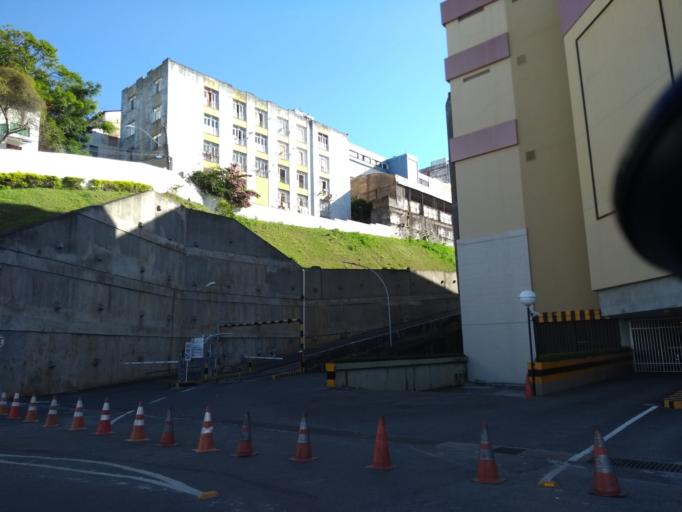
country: BR
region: Bahia
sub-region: Salvador
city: Salvador
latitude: -12.9831
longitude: -38.5124
